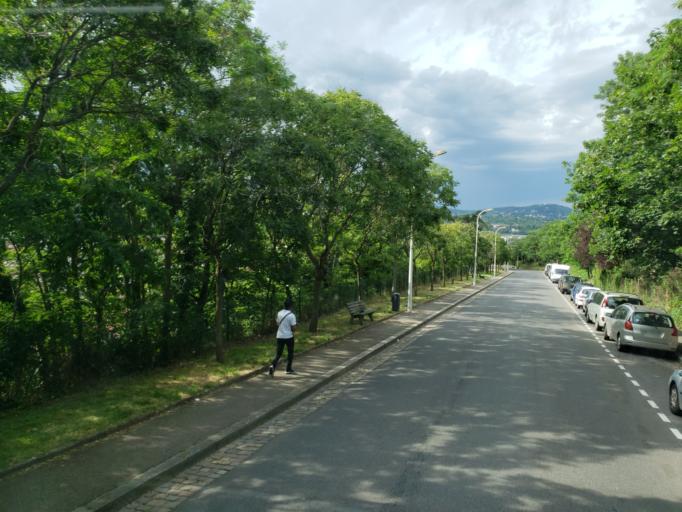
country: FR
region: Rhone-Alpes
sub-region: Departement du Rhone
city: Tassin-la-Demi-Lune
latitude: 45.7708
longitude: 4.8094
